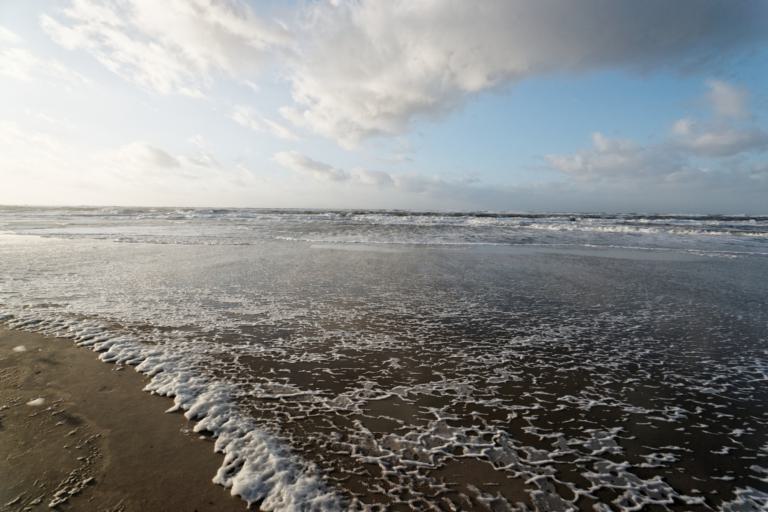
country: NL
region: North Holland
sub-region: Gemeente Texel
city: Den Burg
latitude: 53.0645
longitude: 4.7227
